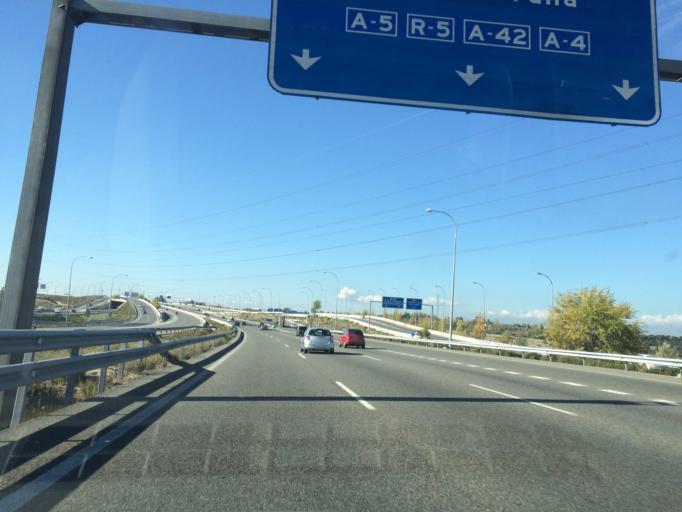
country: ES
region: Madrid
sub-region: Provincia de Madrid
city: Las Tablas
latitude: 40.5182
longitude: -3.6744
